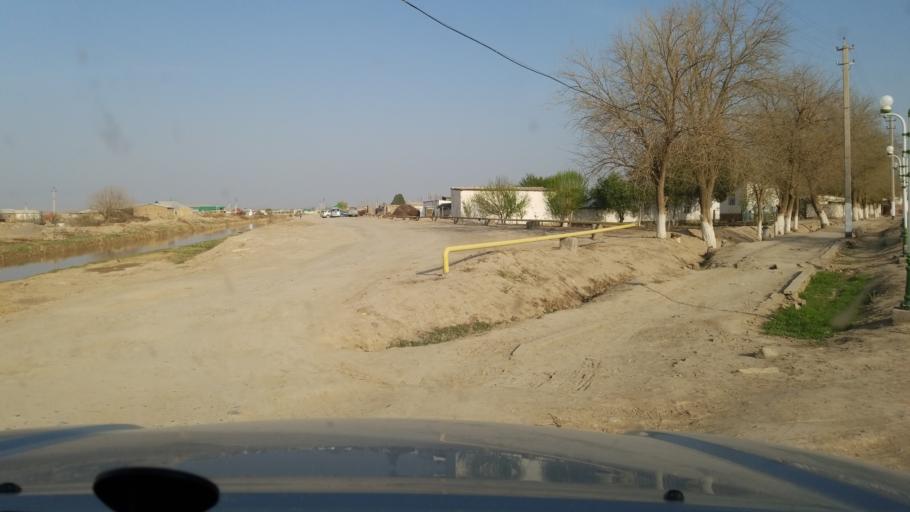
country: AF
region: Jowzjan
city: Qarqin
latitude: 37.5135
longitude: 65.9998
